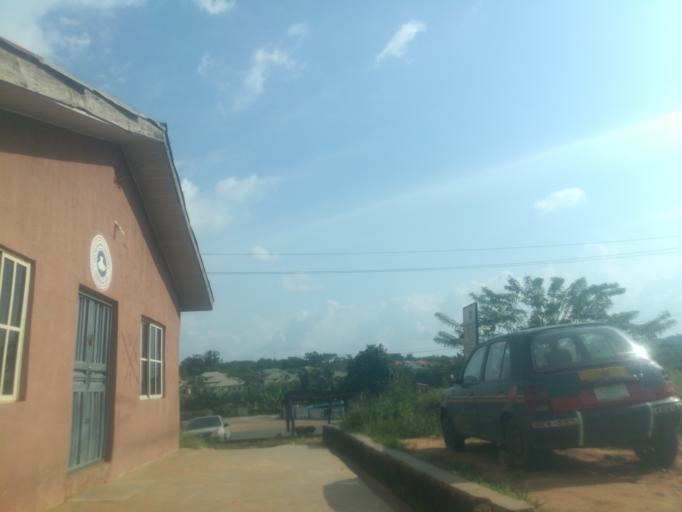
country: NG
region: Oyo
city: Ido
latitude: 7.3973
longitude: 3.7950
